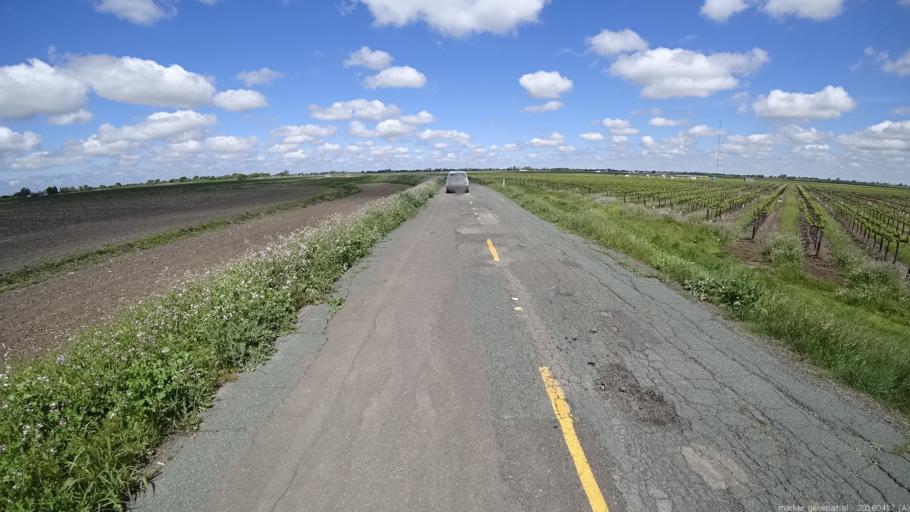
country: US
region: California
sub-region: Sacramento County
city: Walnut Grove
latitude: 38.2035
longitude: -121.5274
